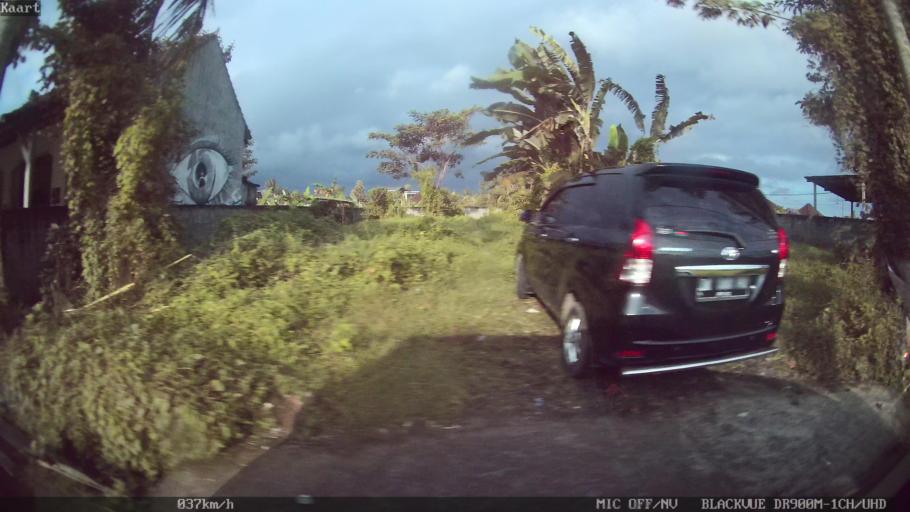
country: ID
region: Bali
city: Banjar Pande
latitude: -8.5156
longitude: 115.2504
